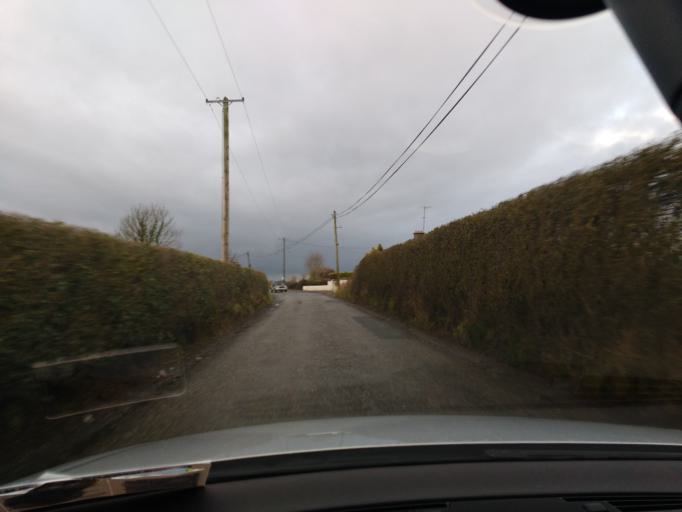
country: IE
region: Munster
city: Thurles
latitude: 52.6380
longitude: -7.8576
